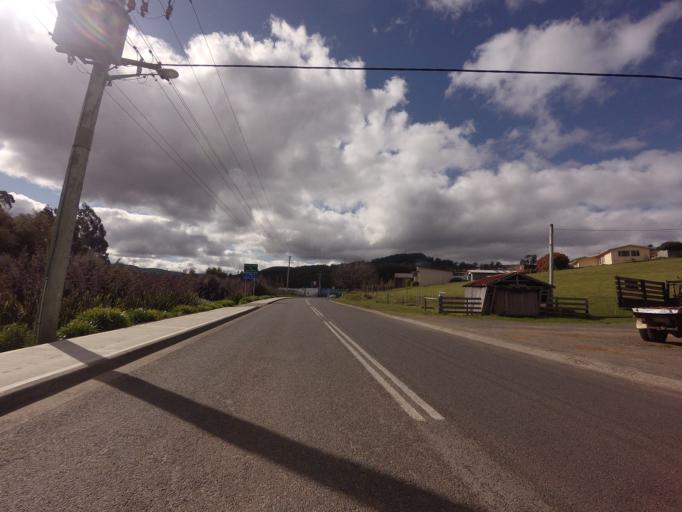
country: AU
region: Tasmania
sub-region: Huon Valley
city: Geeveston
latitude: -43.1659
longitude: 146.9262
